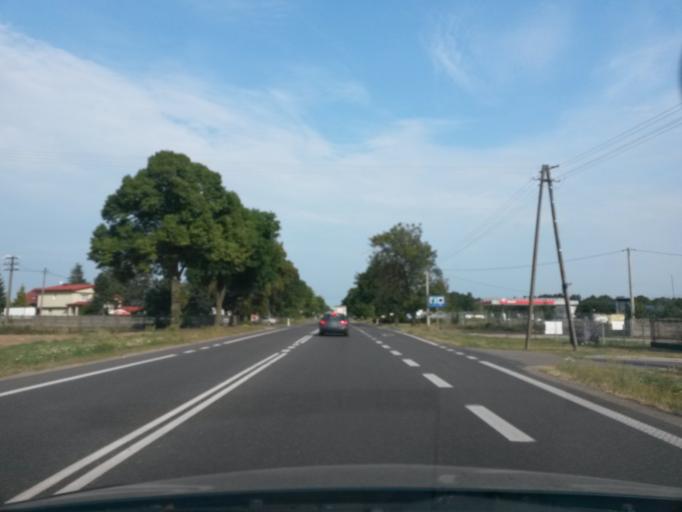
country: PL
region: Masovian Voivodeship
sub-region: Powiat sierpecki
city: Sierpc
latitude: 52.8529
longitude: 19.6898
